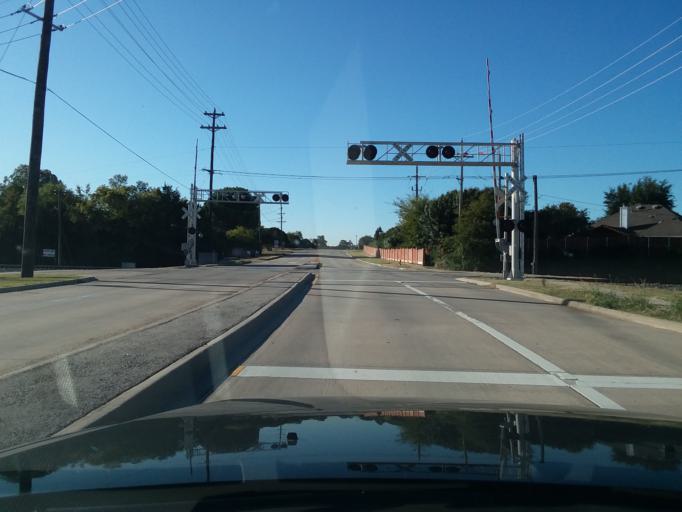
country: US
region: Texas
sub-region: Denton County
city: Highland Village
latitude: 33.0657
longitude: -97.0273
